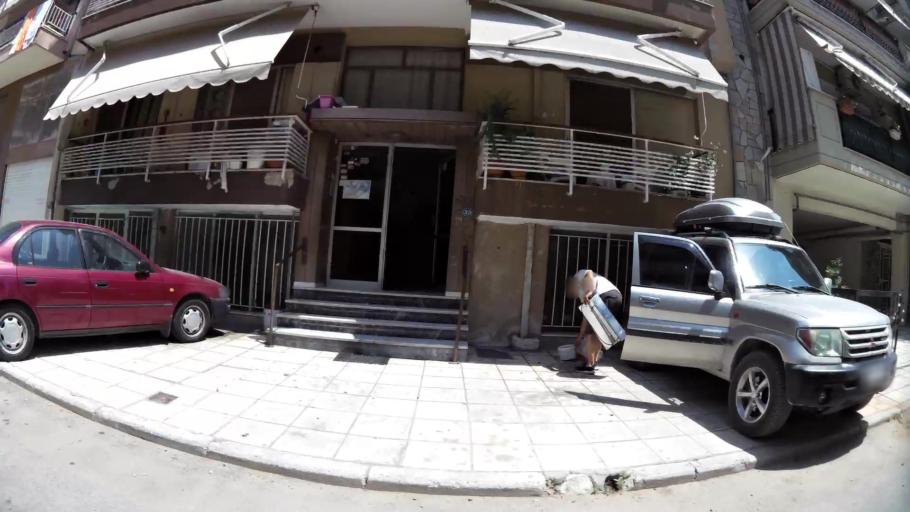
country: GR
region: Central Macedonia
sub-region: Nomos Thessalonikis
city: Menemeni
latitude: 40.6647
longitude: 22.8989
